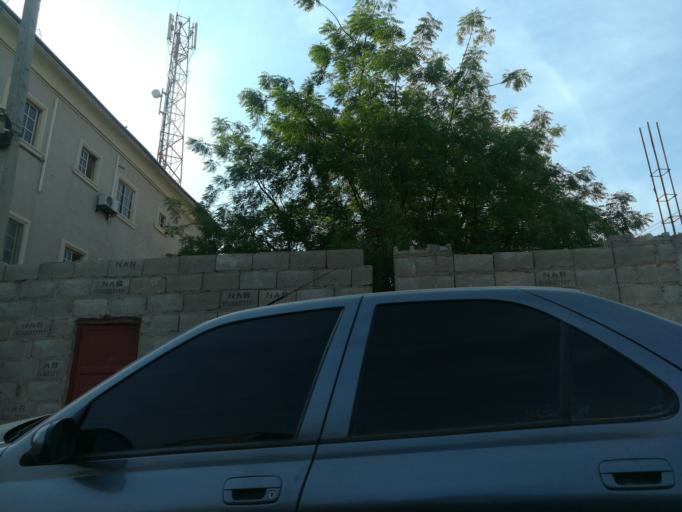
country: NG
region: Kano
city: Kano
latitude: 12.0276
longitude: 8.5257
